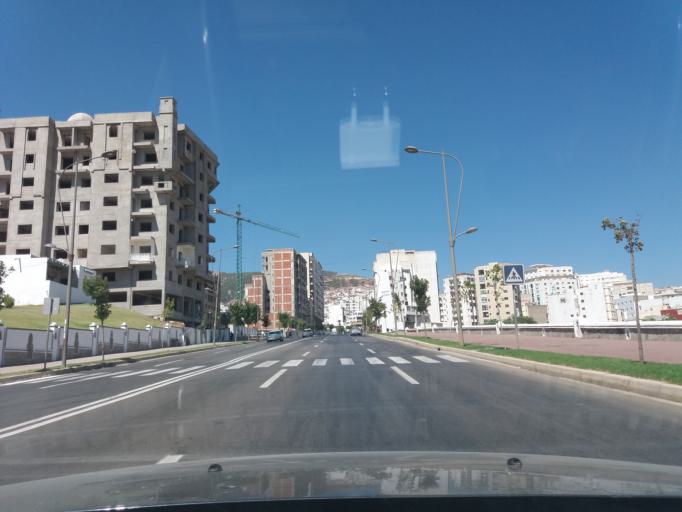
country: MA
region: Tanger-Tetouan
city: Tetouan
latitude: 35.5675
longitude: -5.3898
